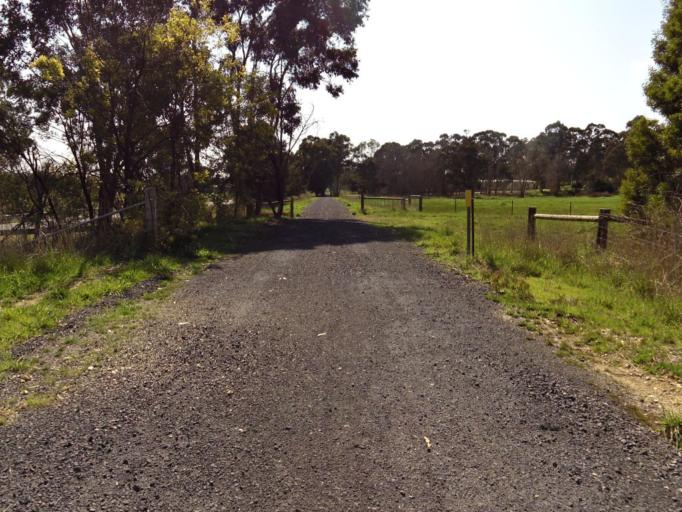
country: AU
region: Victoria
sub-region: Murrindindi
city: Alexandra
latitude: -37.1295
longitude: 145.5954
